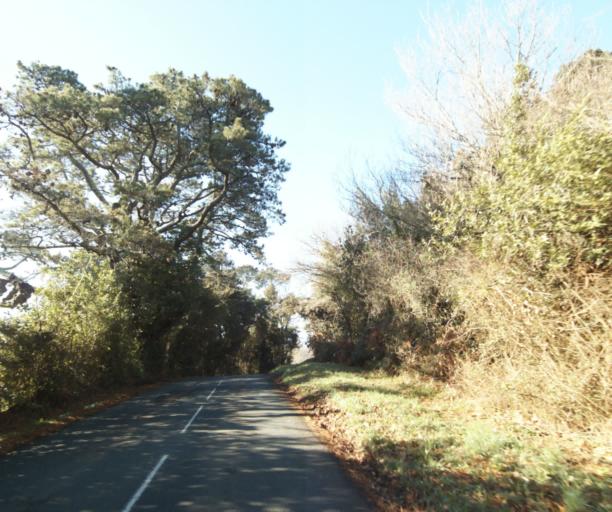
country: FR
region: Aquitaine
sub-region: Departement des Pyrenees-Atlantiques
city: Ciboure
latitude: 43.3616
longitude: -1.6608
